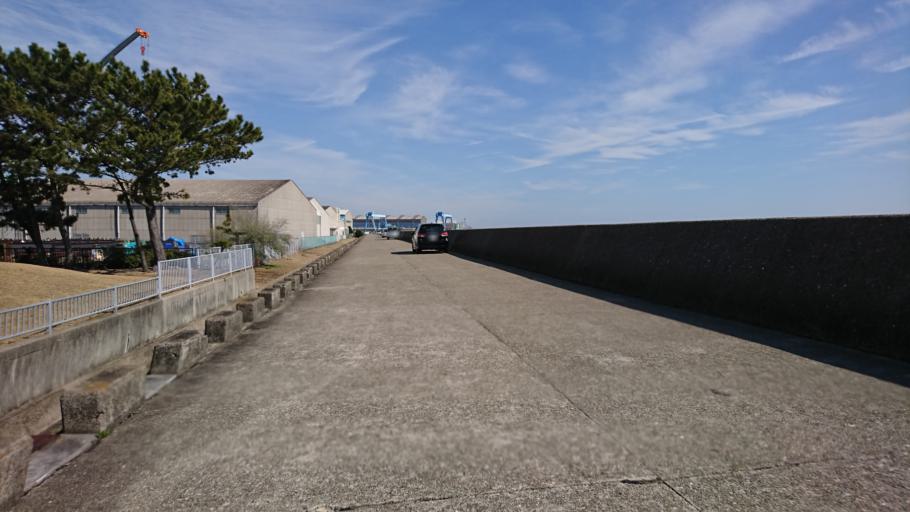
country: JP
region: Hyogo
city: Kakogawacho-honmachi
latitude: 34.6949
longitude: 134.8497
